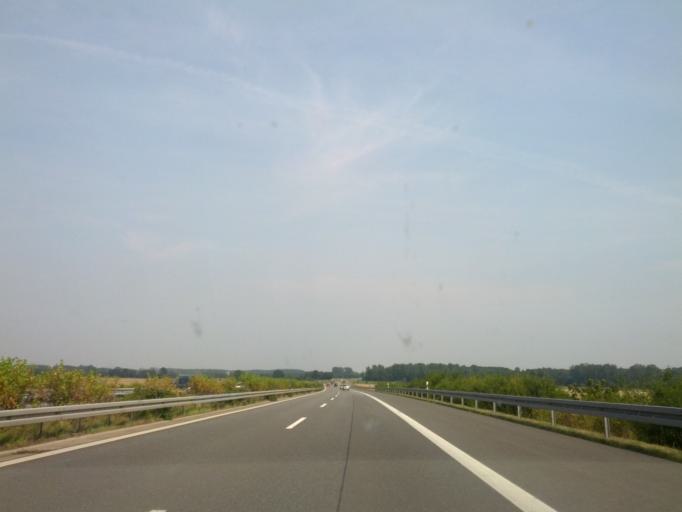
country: DE
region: Mecklenburg-Vorpommern
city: Grimmen
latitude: 54.0825
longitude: 13.0436
